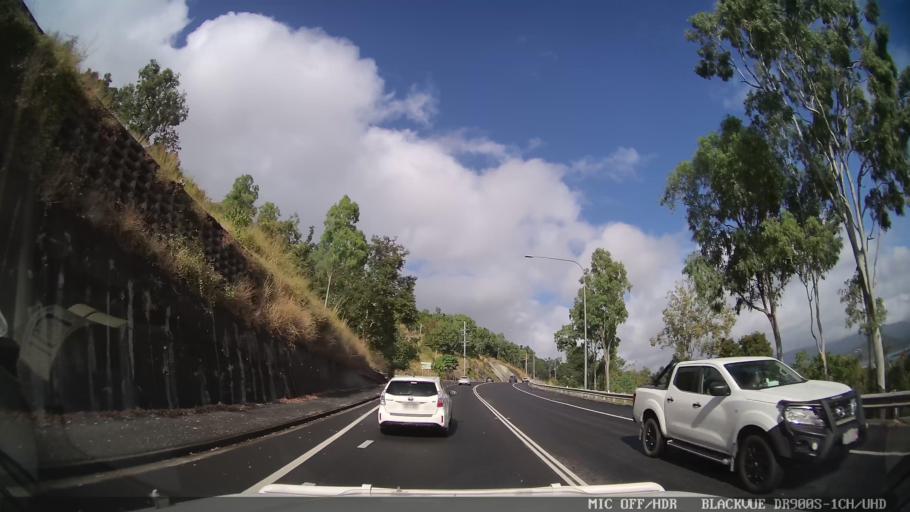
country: AU
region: Queensland
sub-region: Whitsunday
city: Proserpine
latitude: -20.2700
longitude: 148.7106
